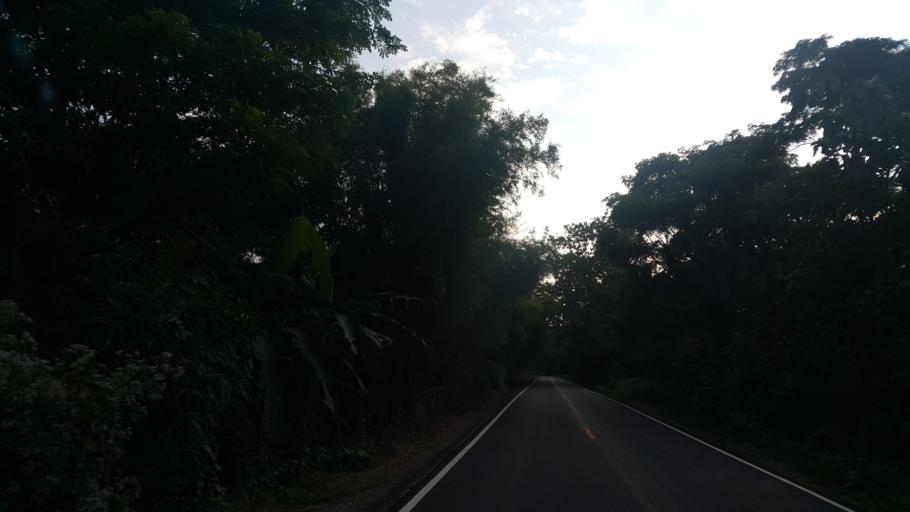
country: TH
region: Lampang
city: Sop Prap
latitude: 17.9334
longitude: 99.3395
